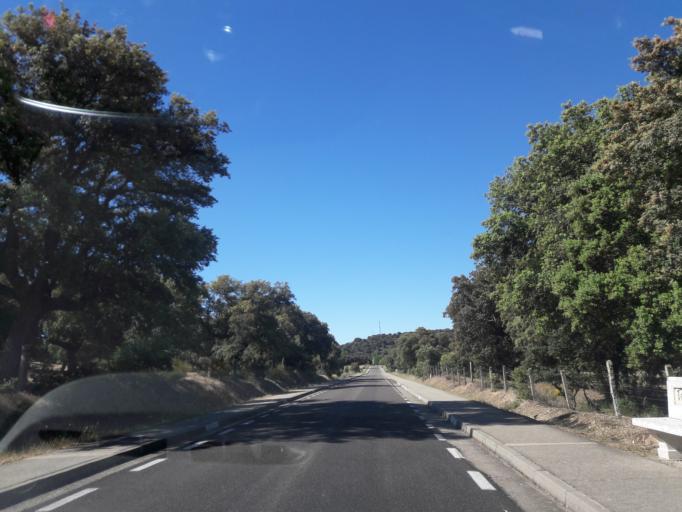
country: ES
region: Castille and Leon
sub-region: Provincia de Salamanca
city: Juzbado
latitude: 41.0778
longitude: -5.8981
